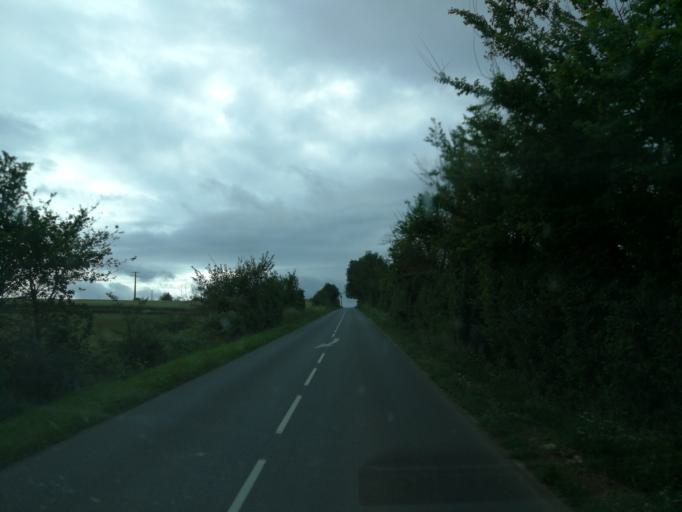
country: FR
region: Pays de la Loire
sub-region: Departement de la Vendee
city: Vix
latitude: 46.3712
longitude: -0.9035
